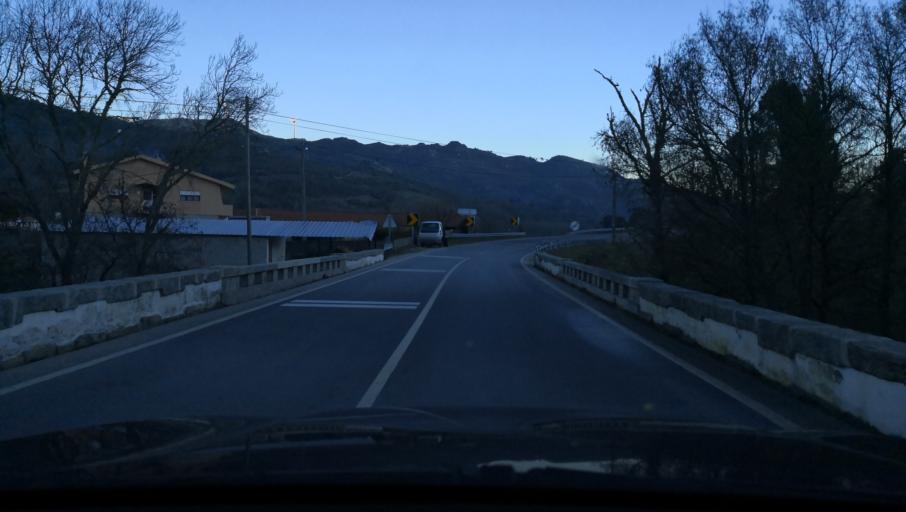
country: PT
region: Vila Real
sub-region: Vila Pouca de Aguiar
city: Vila Pouca de Aguiar
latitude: 41.4211
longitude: -7.6855
